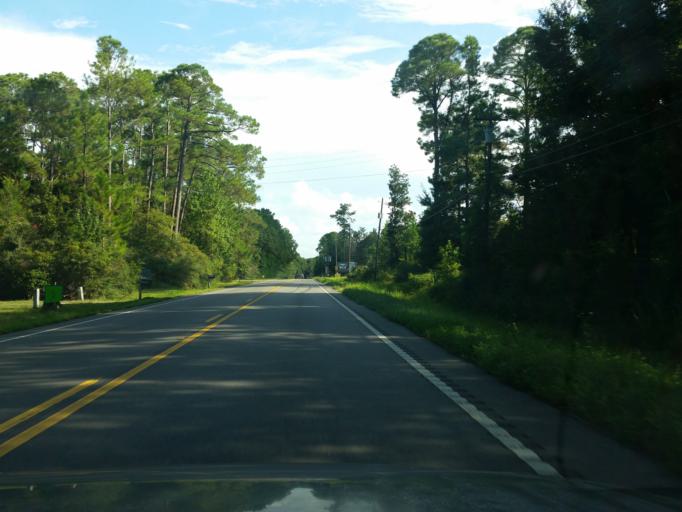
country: US
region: Alabama
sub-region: Mobile County
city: Theodore
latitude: 30.4318
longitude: -88.1081
